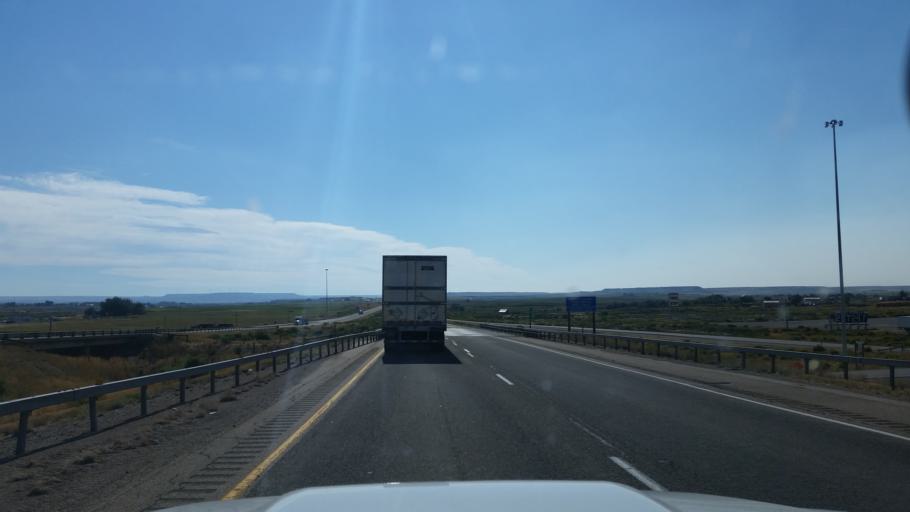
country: US
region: Wyoming
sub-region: Uinta County
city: Lyman
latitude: 41.3672
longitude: -110.2991
